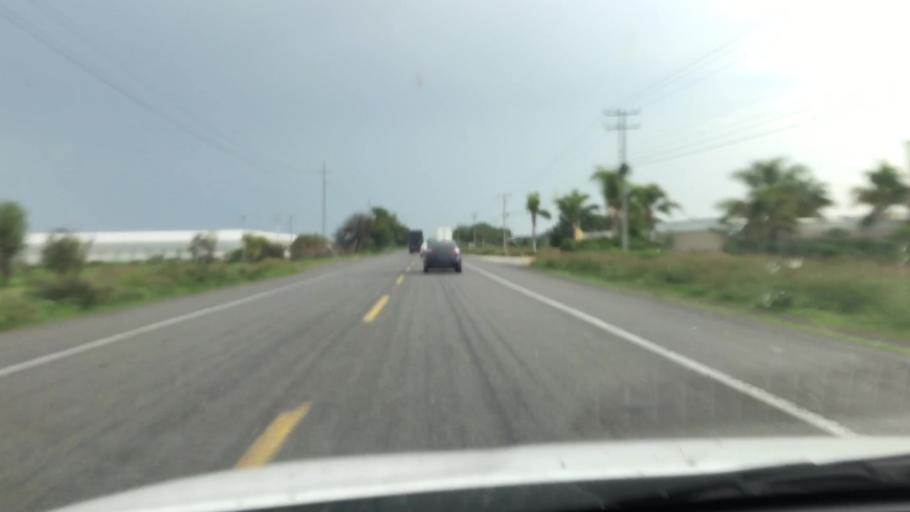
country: MX
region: Michoacan
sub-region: Vista Hermosa
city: Los Pilares
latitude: 20.2759
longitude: -102.3932
